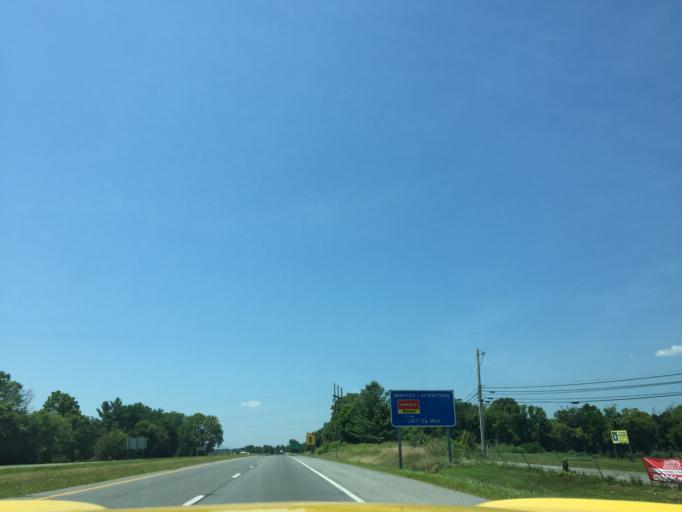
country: US
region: West Virginia
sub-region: Jefferson County
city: Ranson
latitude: 39.3058
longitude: -77.8088
